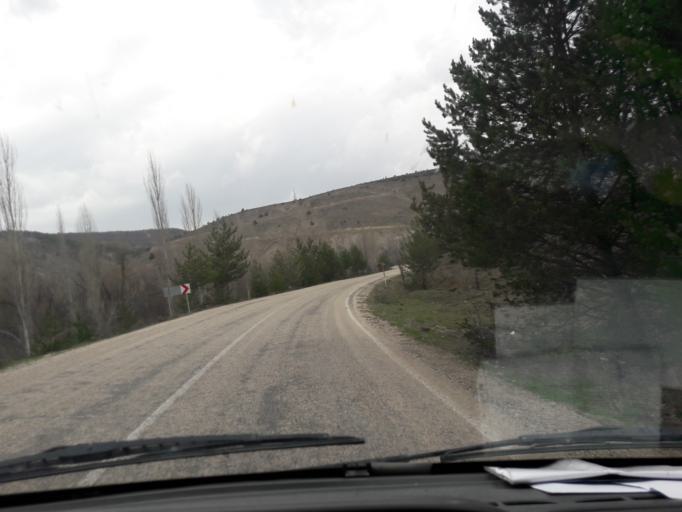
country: TR
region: Giresun
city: Alucra
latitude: 40.2836
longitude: 38.8187
